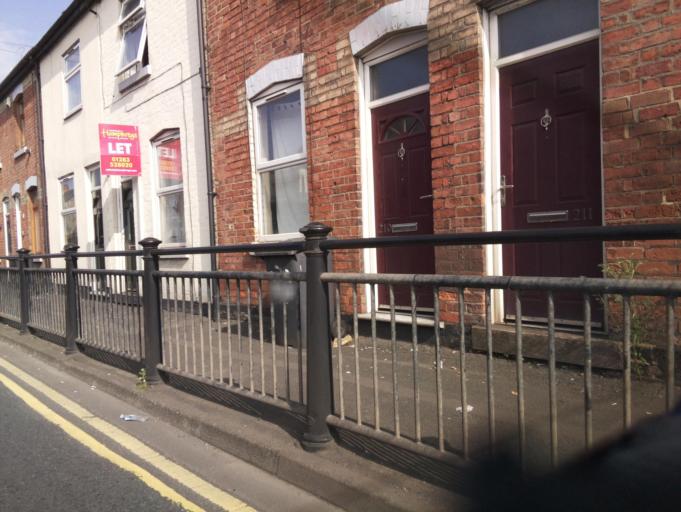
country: GB
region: England
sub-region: Staffordshire
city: Burton upon Trent
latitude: 52.8086
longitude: -1.6421
